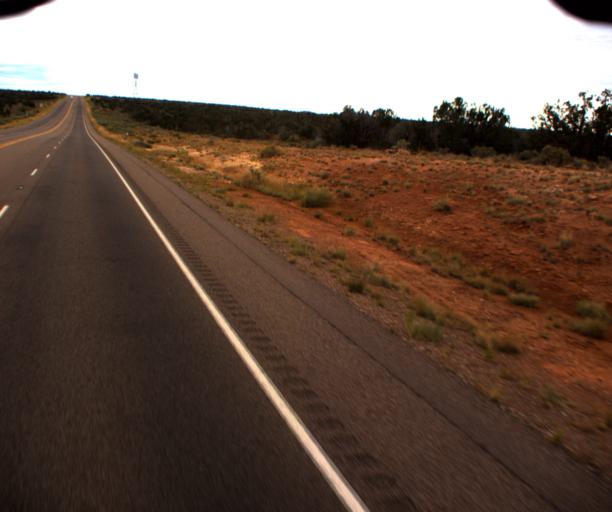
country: US
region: Arizona
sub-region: Navajo County
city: Snowflake
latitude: 34.6424
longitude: -110.0965
